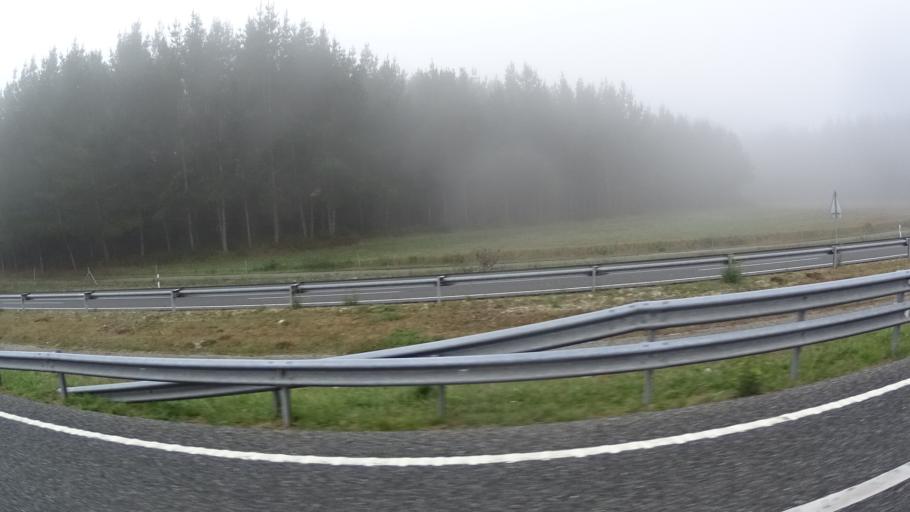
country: ES
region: Galicia
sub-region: Provincia de Lugo
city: Corgo
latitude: 42.9389
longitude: -7.3891
